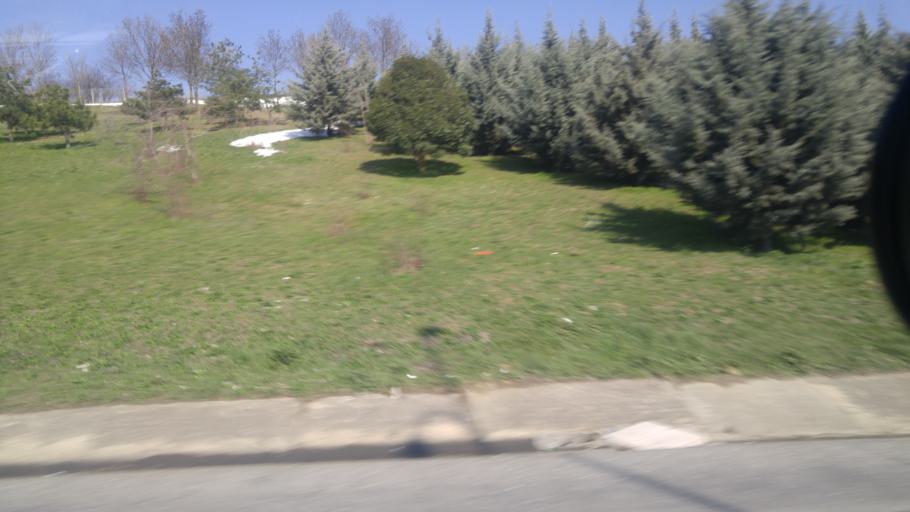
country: TR
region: Istanbul
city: Celaliye
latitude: 41.0536
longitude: 28.4300
